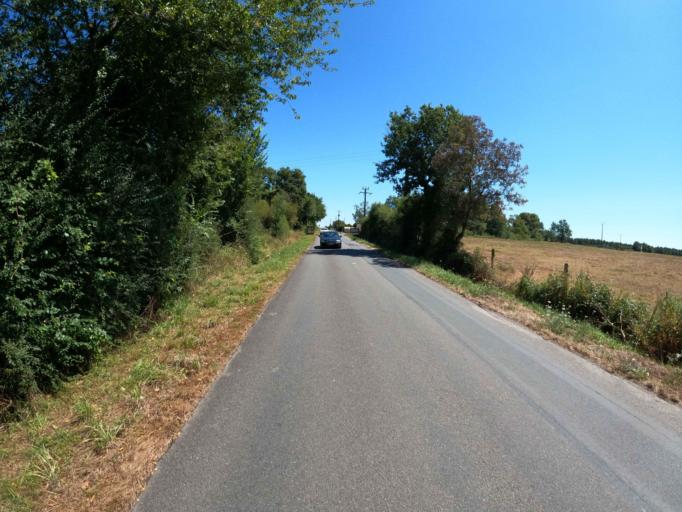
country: FR
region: Pays de la Loire
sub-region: Departement de la Loire-Atlantique
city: La Limouziniere
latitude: 46.9504
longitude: -1.6119
